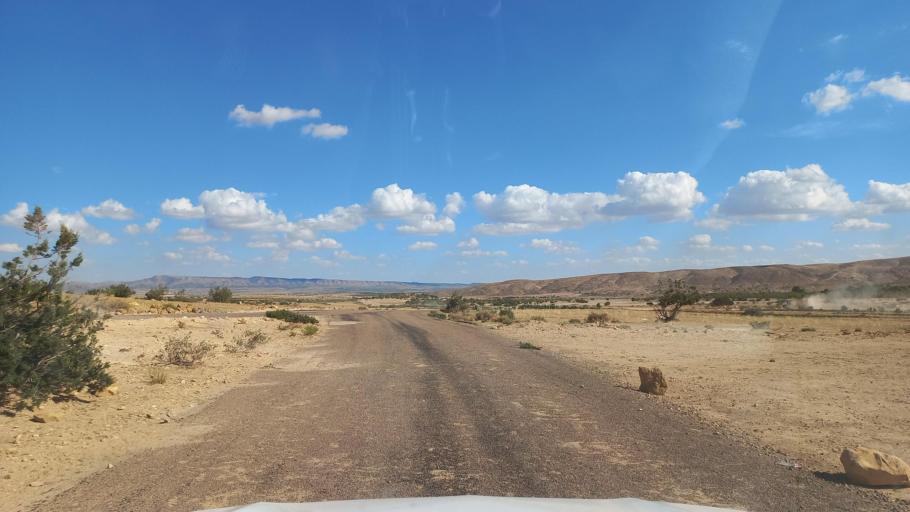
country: TN
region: Al Qasrayn
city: Sbiba
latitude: 35.4047
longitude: 8.9979
